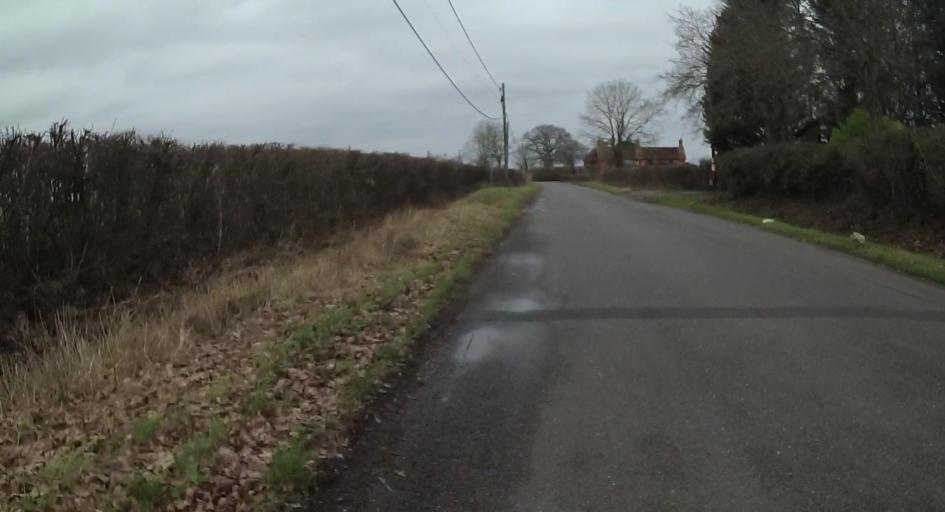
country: GB
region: England
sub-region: West Berkshire
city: Stratfield Mortimer
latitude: 51.3760
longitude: -1.0397
